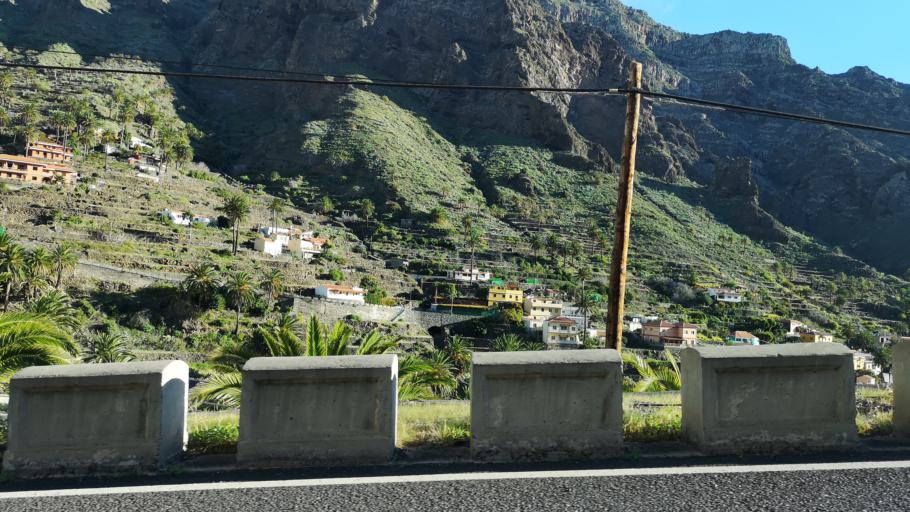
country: ES
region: Canary Islands
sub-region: Provincia de Santa Cruz de Tenerife
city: Vallehermosa
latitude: 28.1154
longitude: -17.3119
